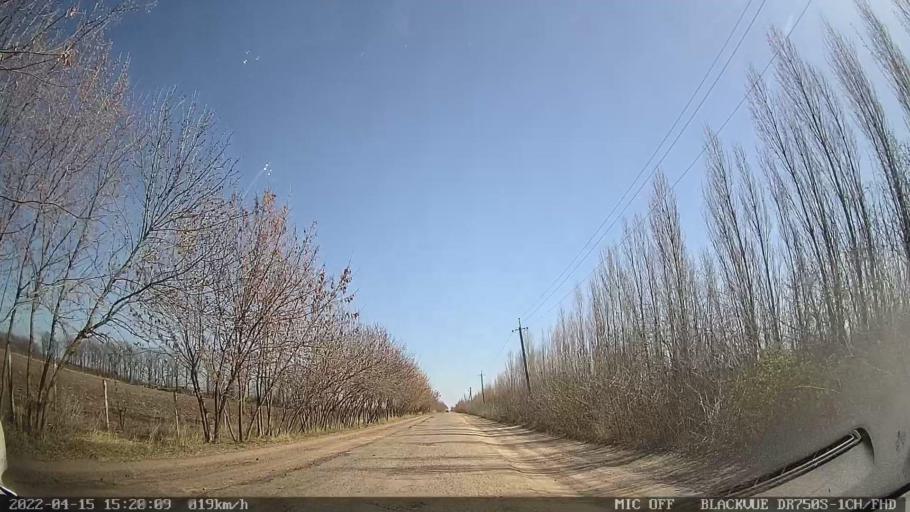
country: MD
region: Raionul Ocnita
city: Otaci
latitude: 48.3866
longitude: 27.9072
